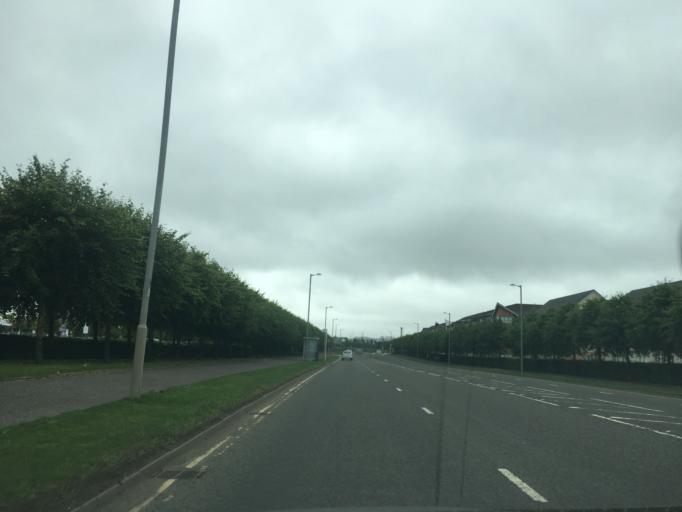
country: GB
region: Scotland
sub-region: Renfrewshire
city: Renfrew
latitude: 55.8784
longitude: -4.3739
